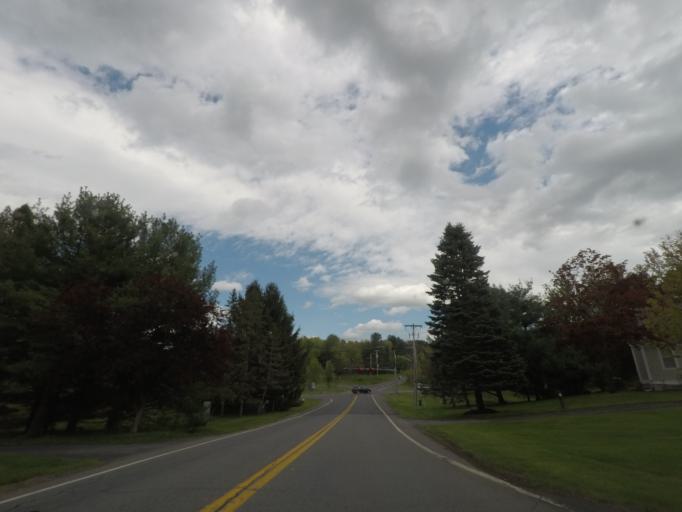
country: US
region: New York
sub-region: Albany County
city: Voorheesville
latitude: 42.6707
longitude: -73.9143
